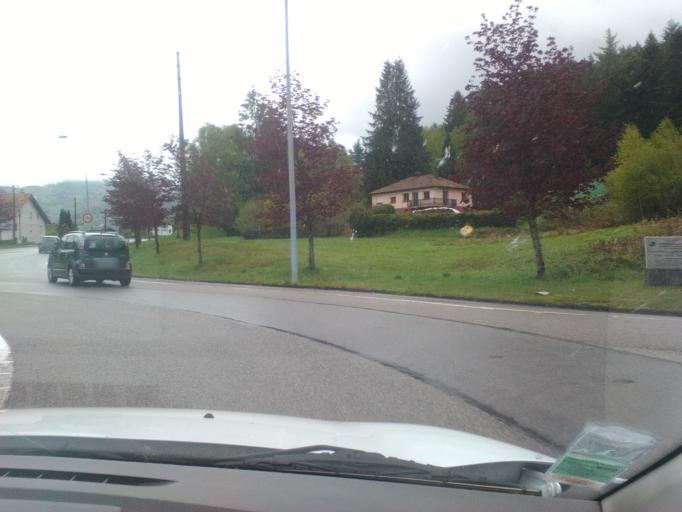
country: FR
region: Lorraine
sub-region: Departement des Vosges
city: Cornimont
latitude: 47.9521
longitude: 6.8178
